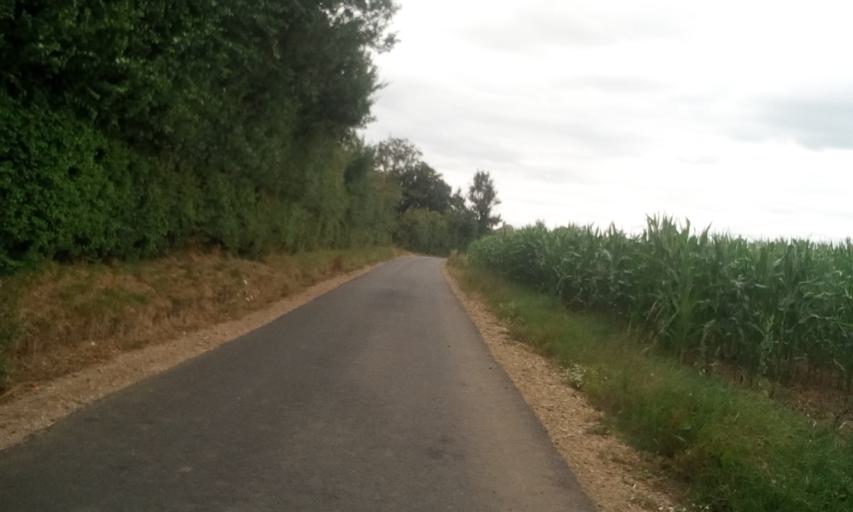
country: FR
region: Lower Normandy
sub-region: Departement du Calvados
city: Thury-Harcourt
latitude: 49.0015
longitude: -0.4417
